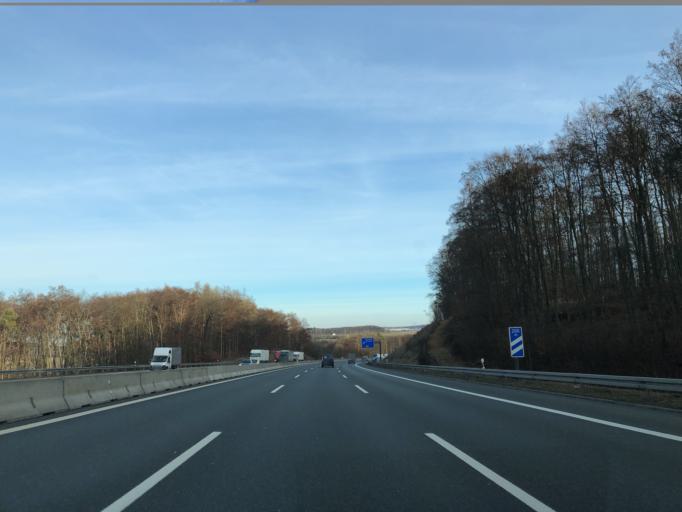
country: DE
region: Bavaria
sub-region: Regierungsbezirk Unterfranken
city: Uettingen
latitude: 49.7700
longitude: 9.7632
